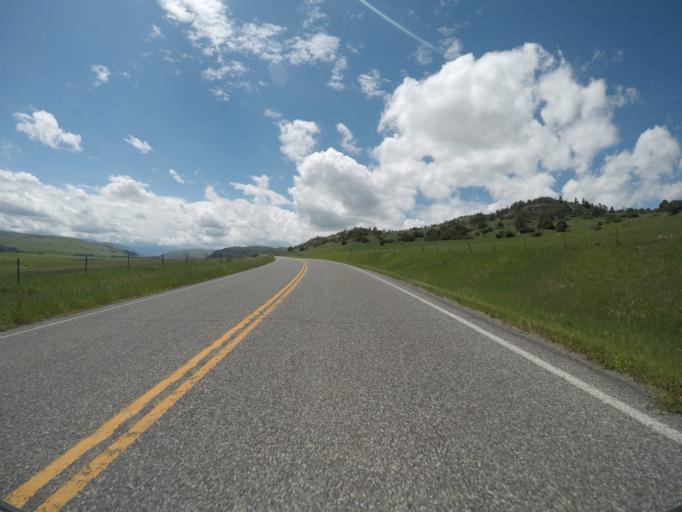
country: US
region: Montana
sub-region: Sweet Grass County
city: Big Timber
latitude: 45.6900
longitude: -110.0692
